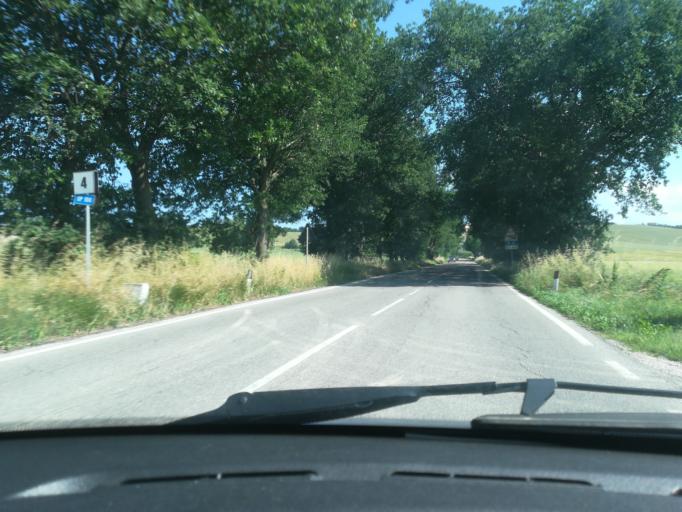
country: IT
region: The Marches
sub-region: Provincia di Macerata
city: Pollenza
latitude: 43.2901
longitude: 13.3804
